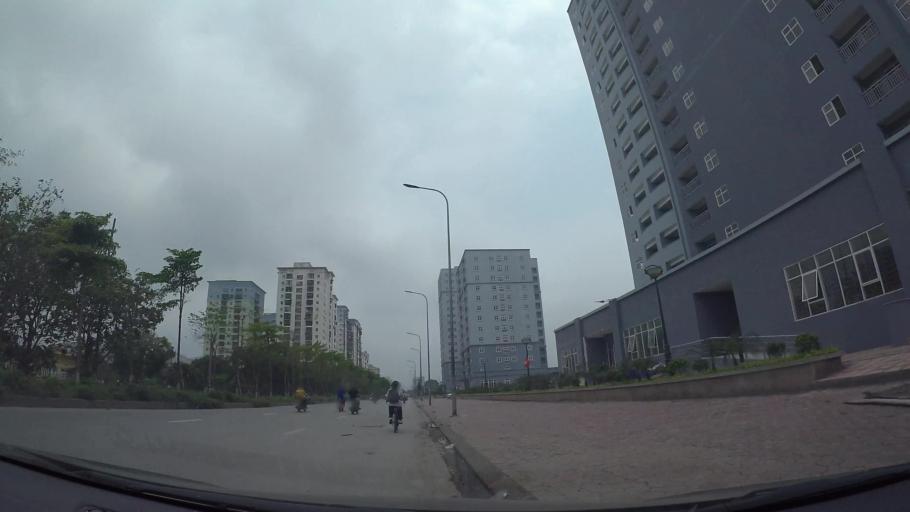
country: VN
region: Ha Noi
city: Hai BaTrung
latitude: 20.9835
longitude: 105.8556
